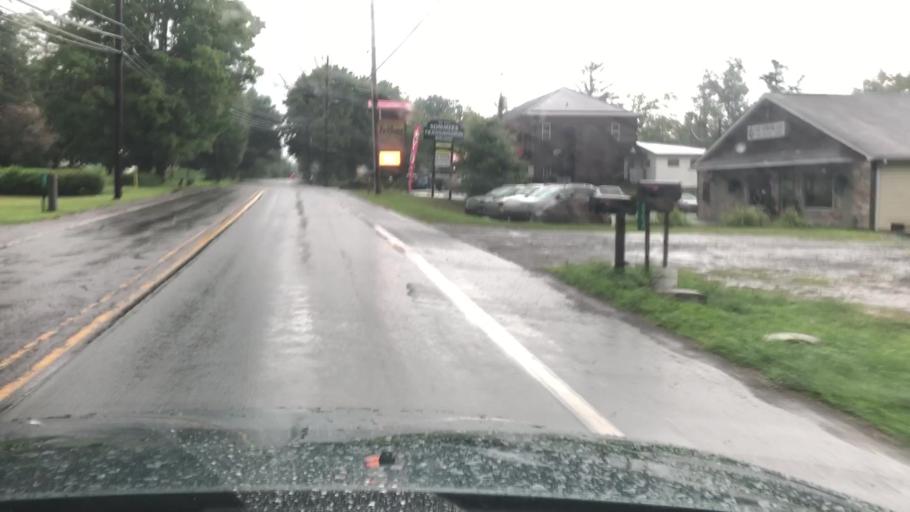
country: US
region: Pennsylvania
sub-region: Monroe County
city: Mountainhome
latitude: 41.1724
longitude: -75.2711
